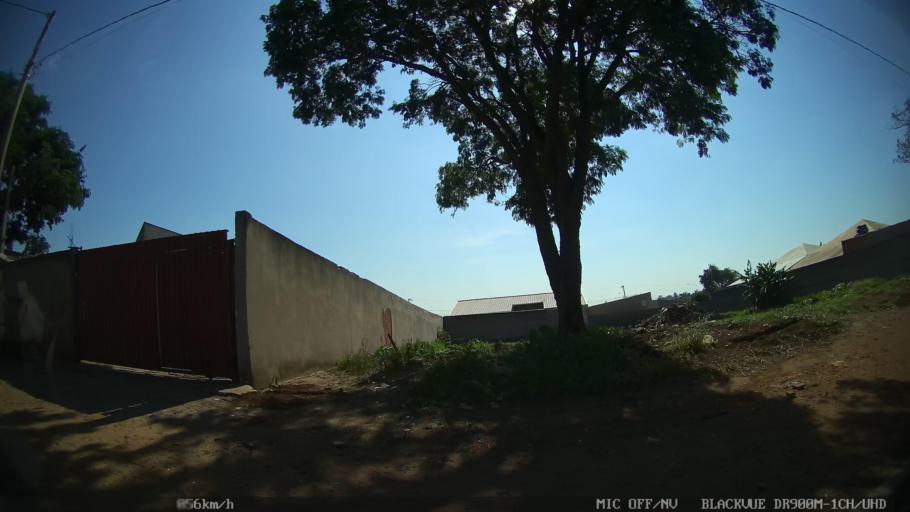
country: BR
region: Sao Paulo
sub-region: Indaiatuba
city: Indaiatuba
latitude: -23.0324
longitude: -47.1026
